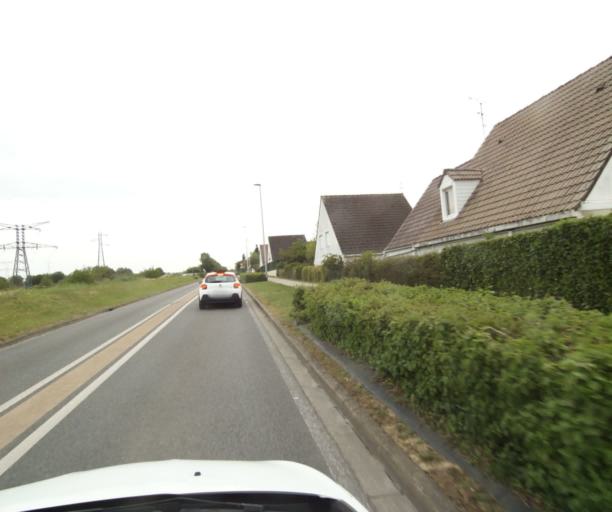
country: FR
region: Ile-de-France
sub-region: Departement de Seine-et-Marne
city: Torcy
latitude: 48.8534
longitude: 2.6592
